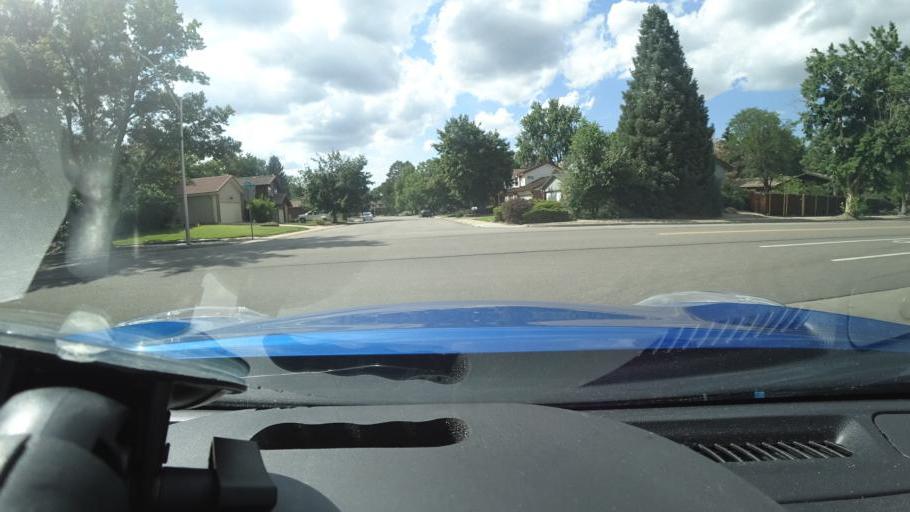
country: US
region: Colorado
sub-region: Adams County
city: Aurora
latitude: 39.6871
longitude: -104.8550
